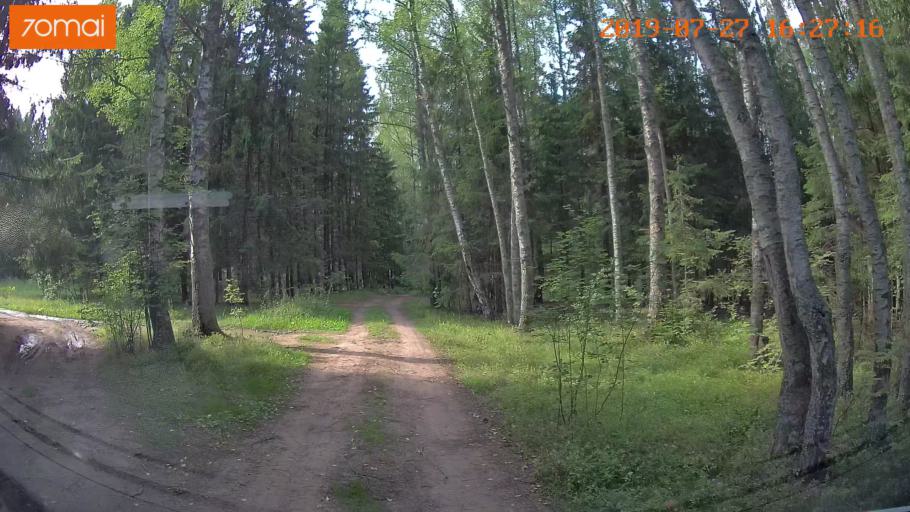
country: RU
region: Ivanovo
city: Novo-Talitsy
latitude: 57.0924
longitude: 40.8534
